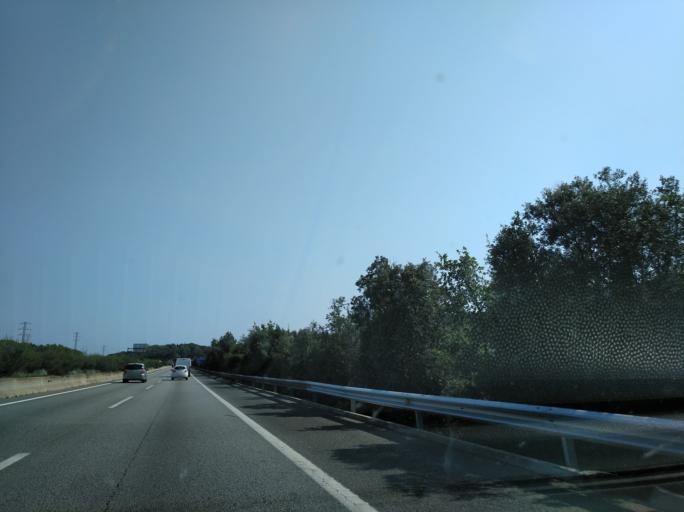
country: ES
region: Catalonia
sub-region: Provincia de Barcelona
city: Argentona
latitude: 41.5676
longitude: 2.3962
